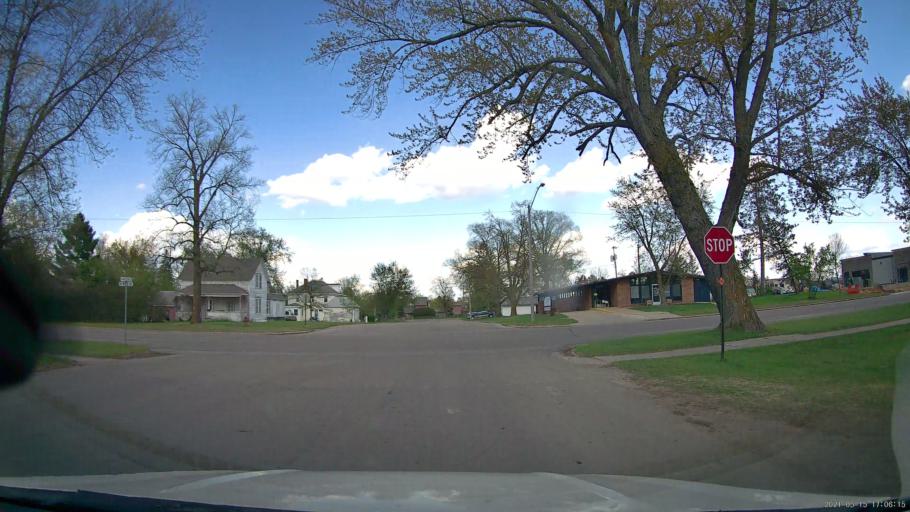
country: US
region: Minnesota
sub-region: Hubbard County
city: Park Rapids
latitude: 46.9235
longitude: -95.0605
